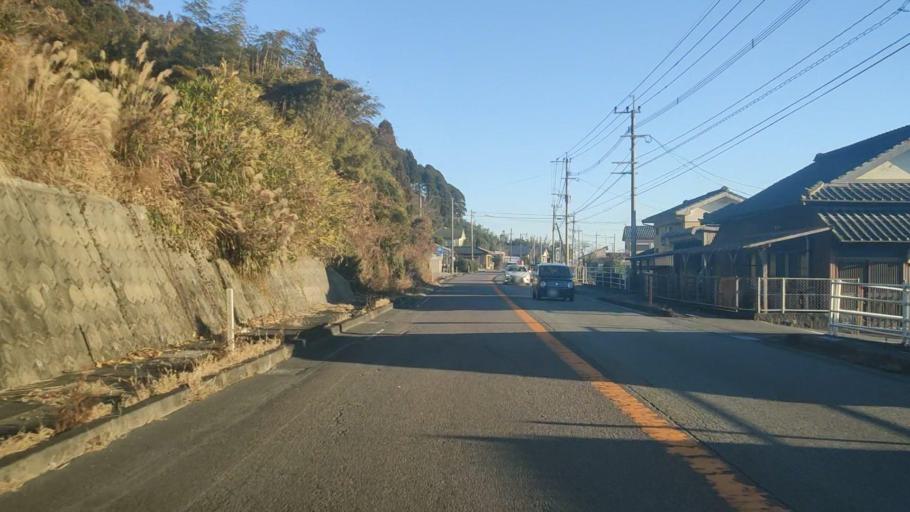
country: JP
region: Miyazaki
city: Takanabe
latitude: 32.0834
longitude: 131.5104
